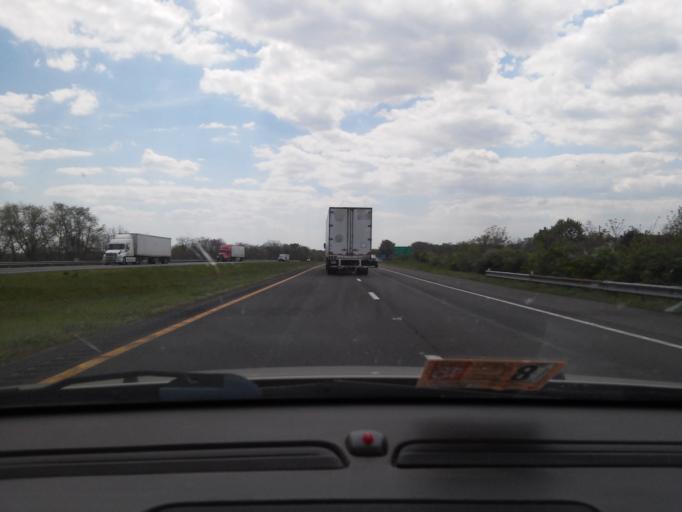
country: US
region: Virginia
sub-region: City of Winchester
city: Winchester
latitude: 39.2475
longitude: -78.1087
